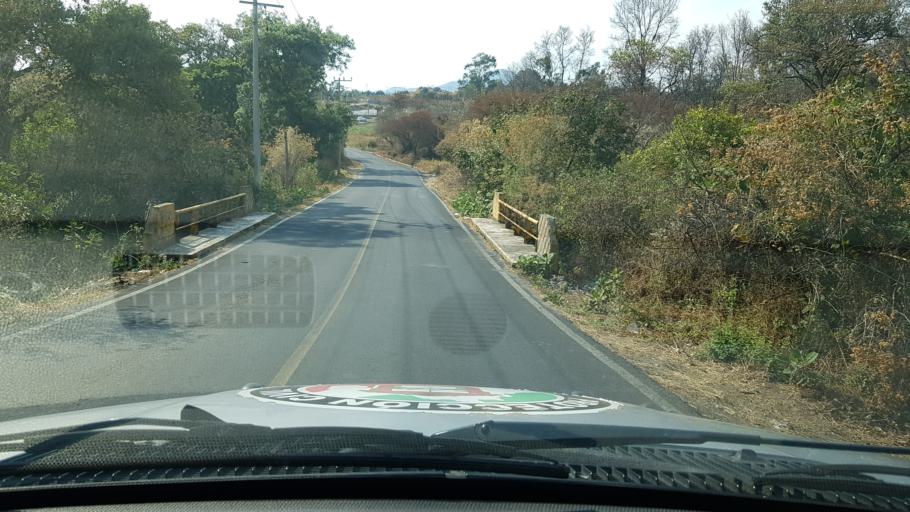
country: MX
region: Mexico
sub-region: Ozumba
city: San Jose Tlacotitlan
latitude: 18.9902
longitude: -98.8228
